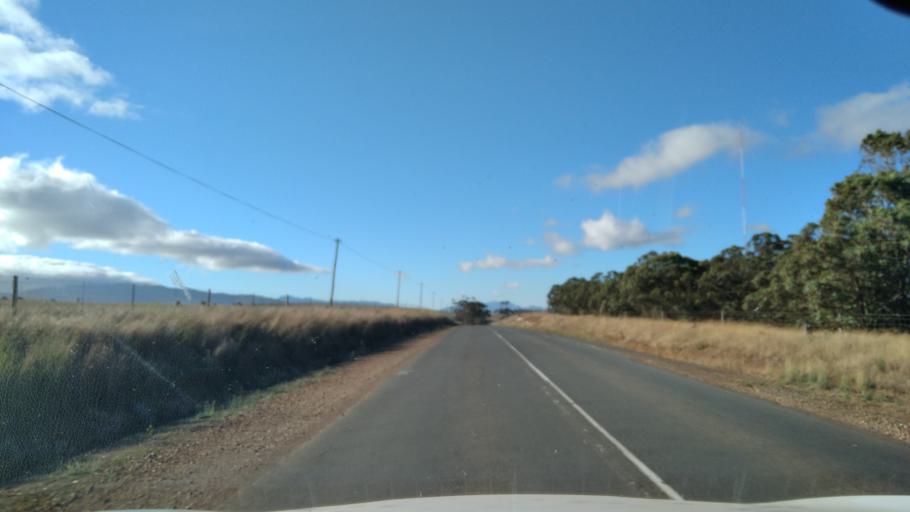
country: ZA
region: Western Cape
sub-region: Overberg District Municipality
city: Caledon
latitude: -34.2168
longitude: 19.2761
